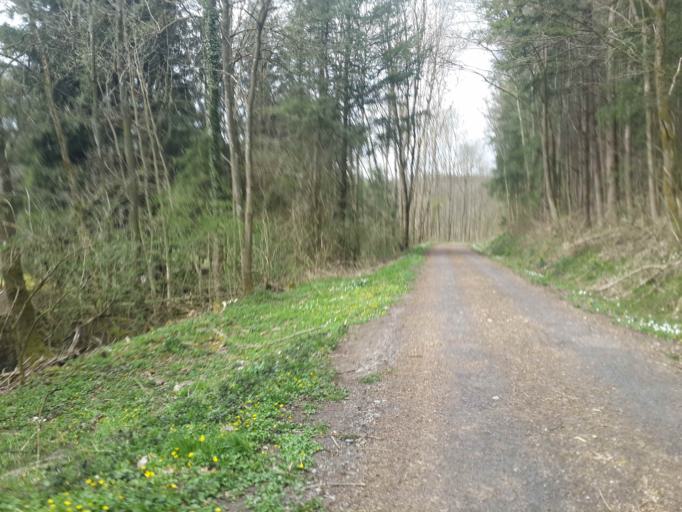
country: DE
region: Baden-Wuerttemberg
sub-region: Karlsruhe Region
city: Billigheim
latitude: 49.3351
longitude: 9.2481
